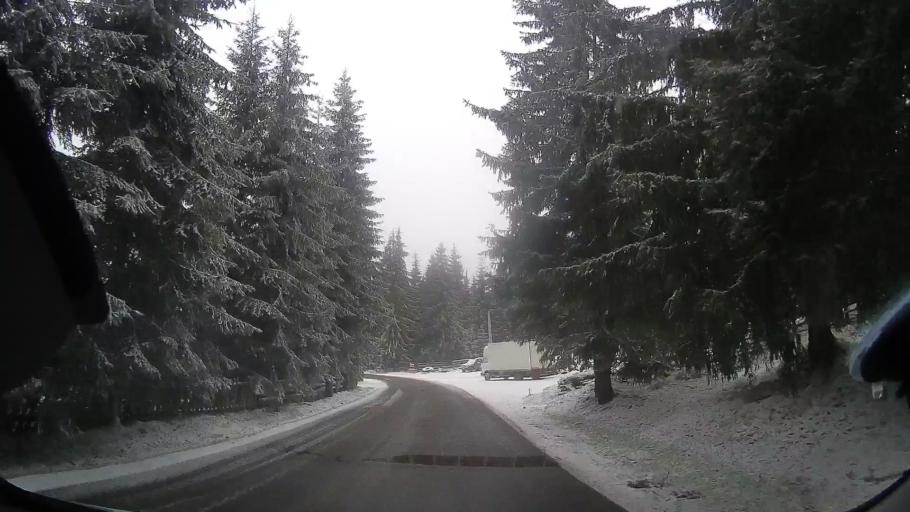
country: RO
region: Cluj
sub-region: Comuna Maguri-Racatau
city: Maguri
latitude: 46.6596
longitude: 23.0972
